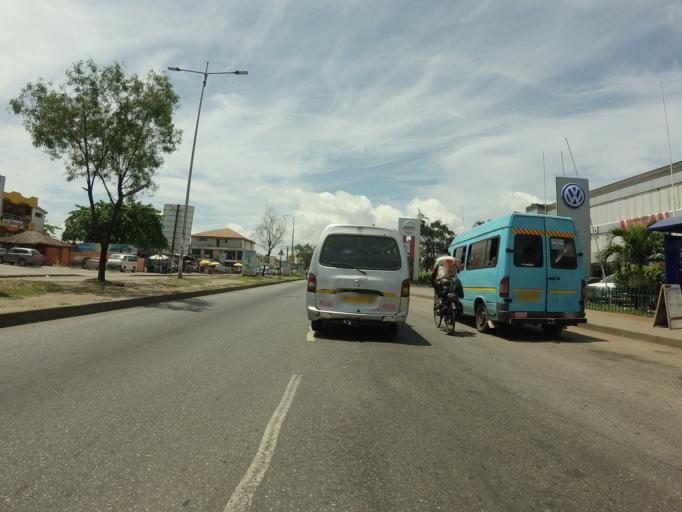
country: GH
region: Greater Accra
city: Accra
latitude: 5.5604
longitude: -0.2276
